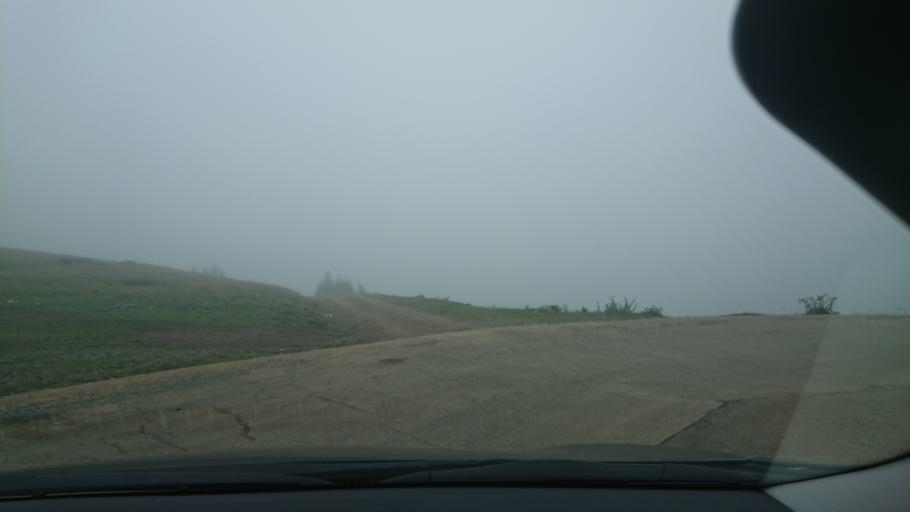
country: TR
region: Gumushane
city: Kurtun
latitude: 40.6716
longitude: 39.0118
